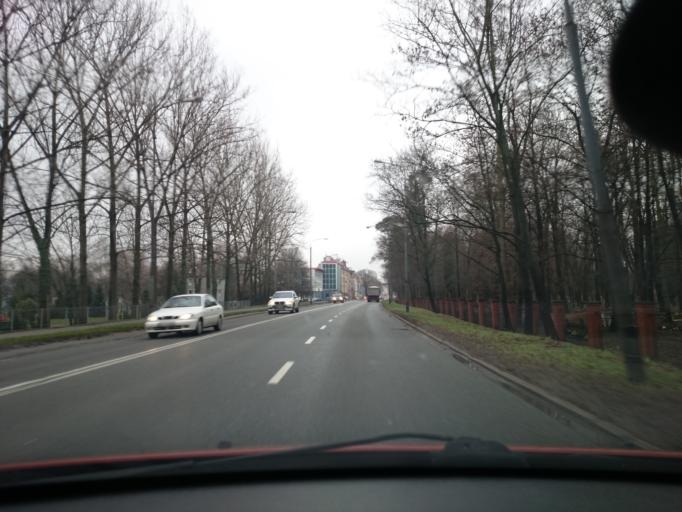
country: PL
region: Opole Voivodeship
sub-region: Powiat opolski
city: Opole
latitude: 50.6759
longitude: 17.9071
